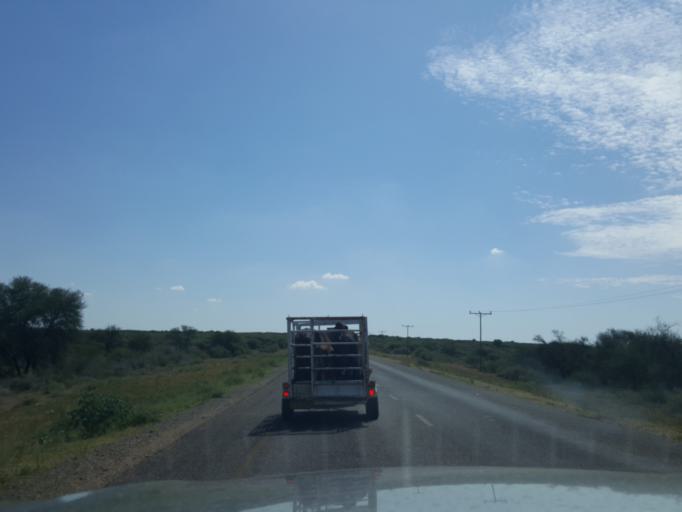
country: BW
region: Kweneng
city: Letlhakeng
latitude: -24.1183
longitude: 25.0574
